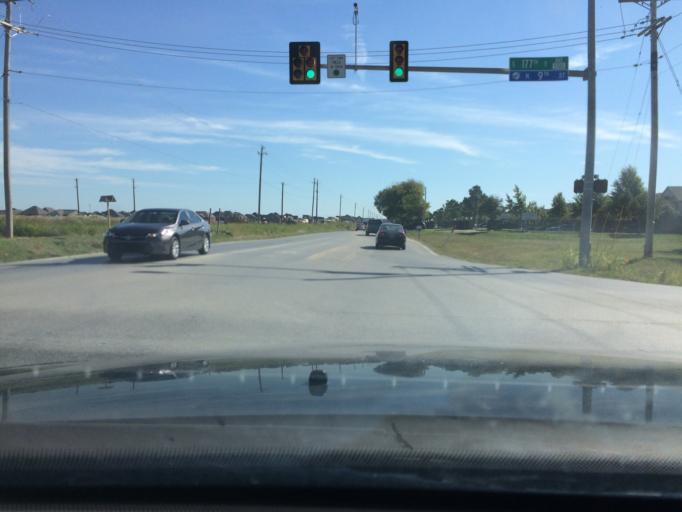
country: US
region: Oklahoma
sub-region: Tulsa County
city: Broken Arrow
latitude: 36.0900
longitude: -95.7797
